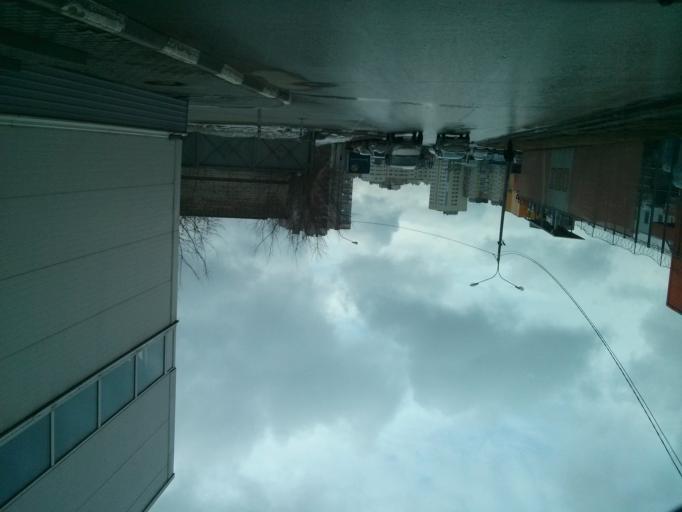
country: RU
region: Nizjnij Novgorod
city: Bor
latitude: 56.3076
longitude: 44.0717
